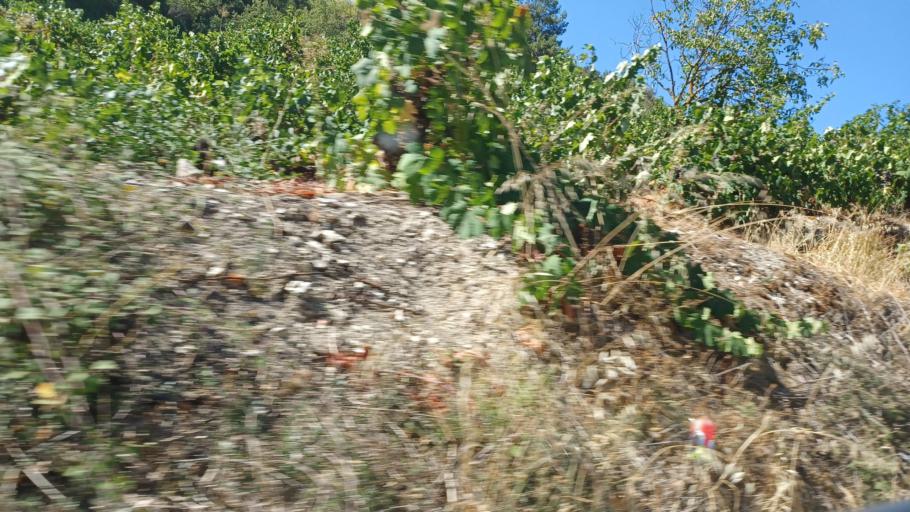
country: CY
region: Pafos
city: Mesogi
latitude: 34.9096
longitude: 32.6256
